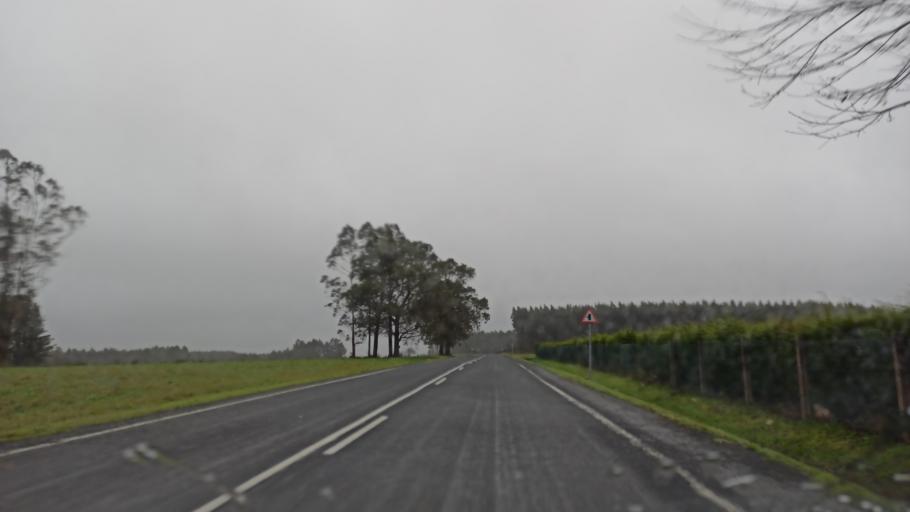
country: ES
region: Galicia
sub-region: Provincia da Coruna
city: Coiros
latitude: 43.1781
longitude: -8.1188
